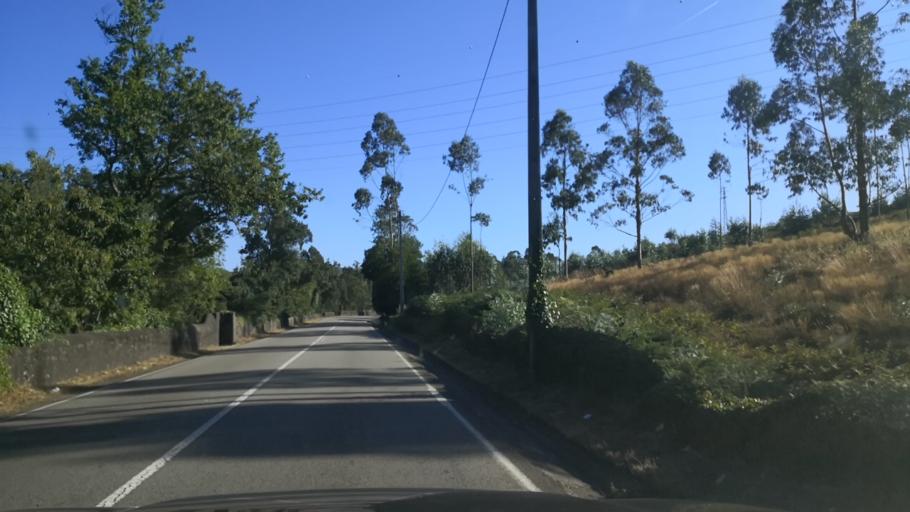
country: PT
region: Porto
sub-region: Pacos de Ferreira
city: Seroa
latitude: 41.2709
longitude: -8.4700
